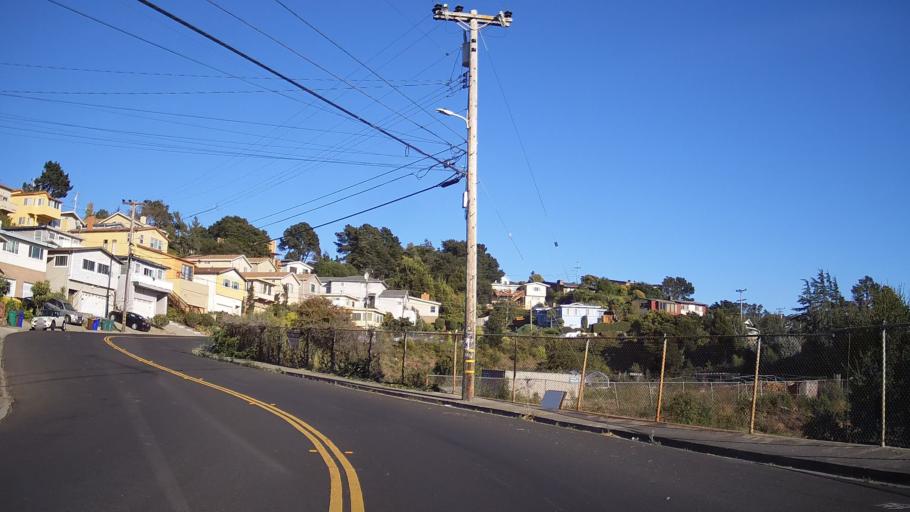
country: US
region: California
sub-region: Contra Costa County
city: East Richmond Heights
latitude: 37.9460
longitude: -122.3174
